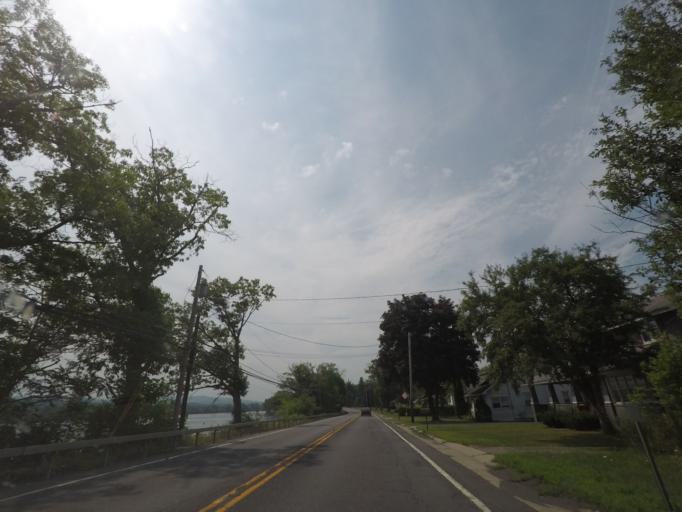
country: US
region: New York
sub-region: Saratoga County
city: Mechanicville
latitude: 42.8599
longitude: -73.6779
